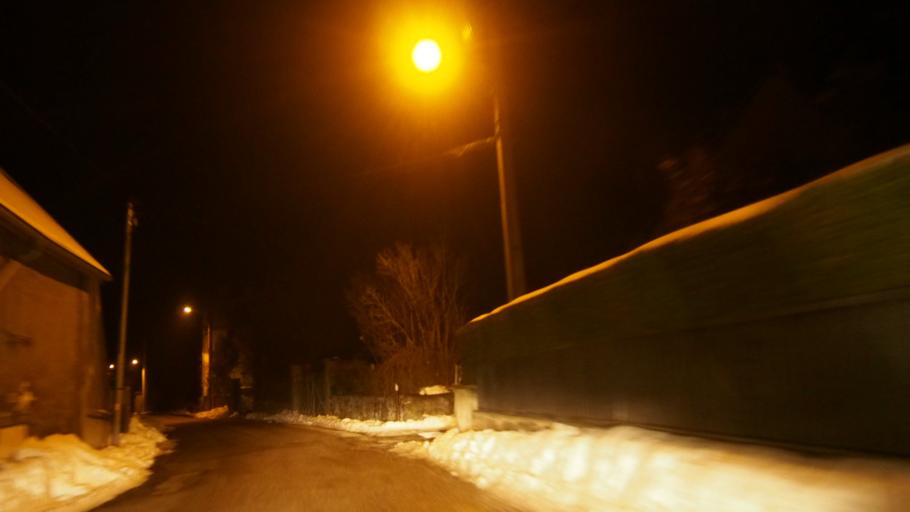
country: FR
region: Rhone-Alpes
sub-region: Departement de l'Isere
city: Pierre-Chatel
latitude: 44.9830
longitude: 5.7838
